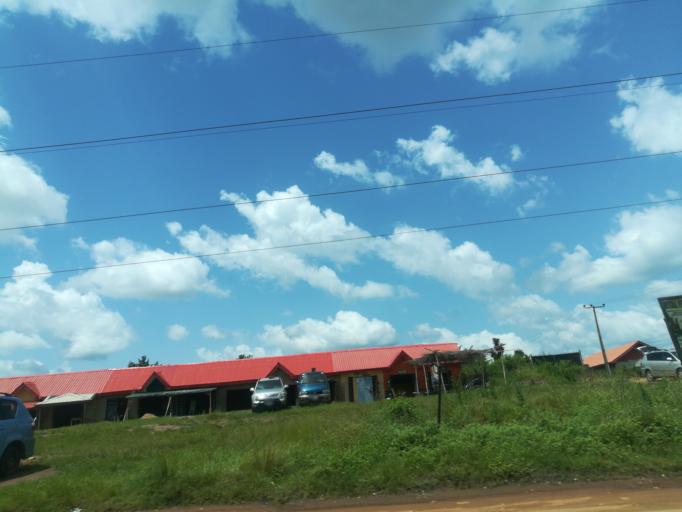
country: NG
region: Oyo
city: Lalupon
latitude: 7.4406
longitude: 4.0074
